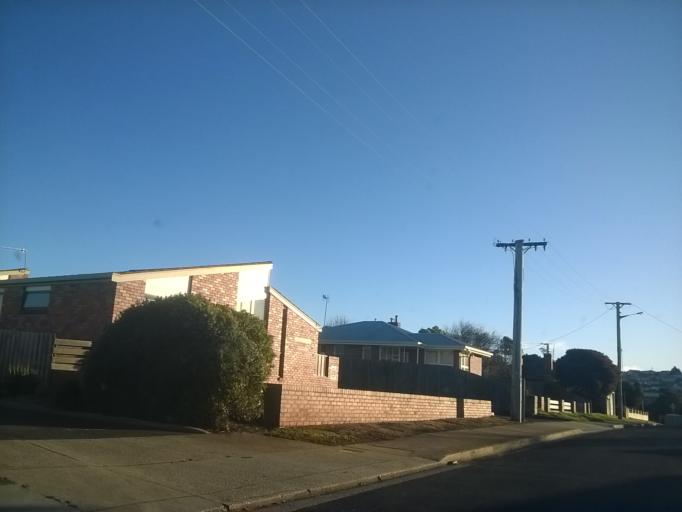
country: AU
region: Tasmania
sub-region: Burnie
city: Burnie
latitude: -41.0677
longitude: 145.9027
